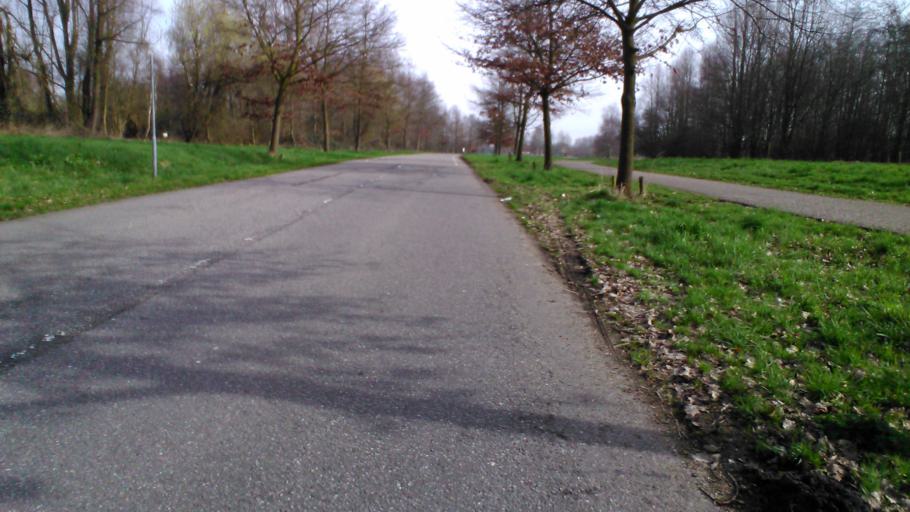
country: NL
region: South Holland
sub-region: Gemeente Lansingerland
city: Bleiswijk
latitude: 51.9714
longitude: 4.5497
